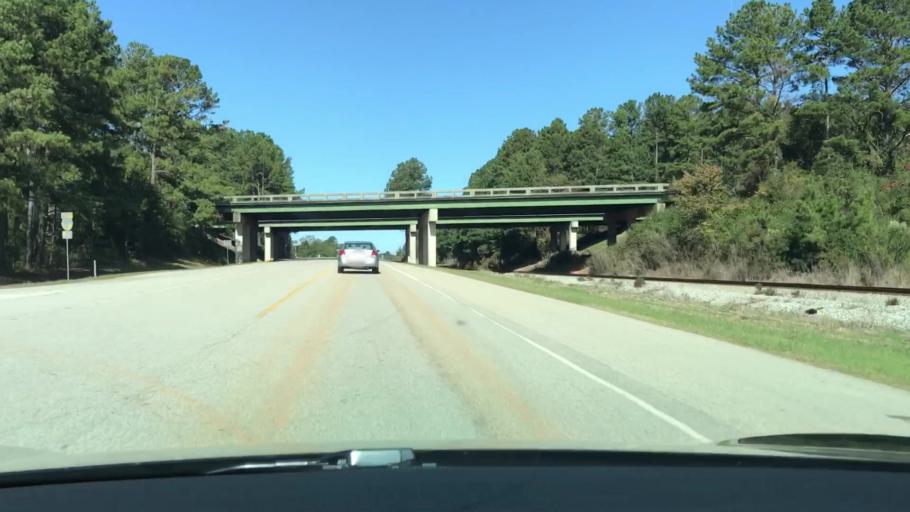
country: US
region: Georgia
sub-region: Taliaferro County
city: Crawfordville
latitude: 33.4980
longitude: -82.8034
